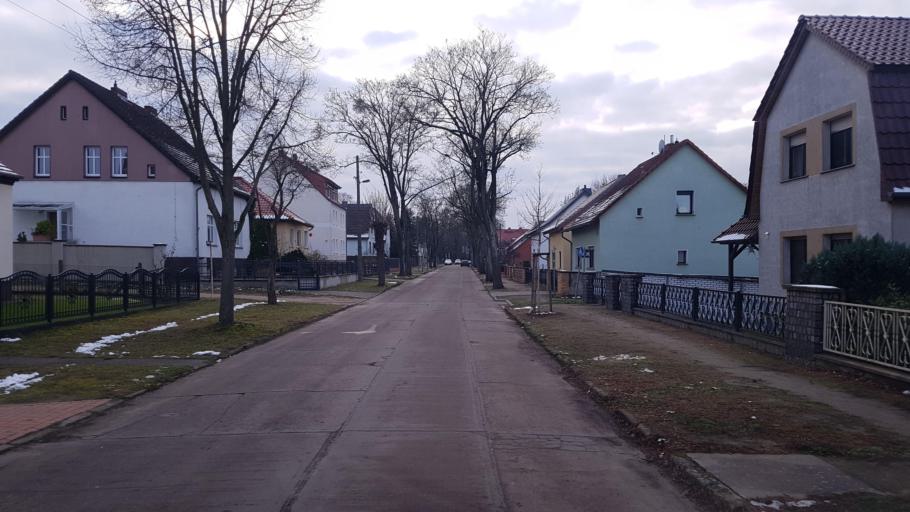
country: DE
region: Brandenburg
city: Rehfelde
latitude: 52.5108
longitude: 13.8558
